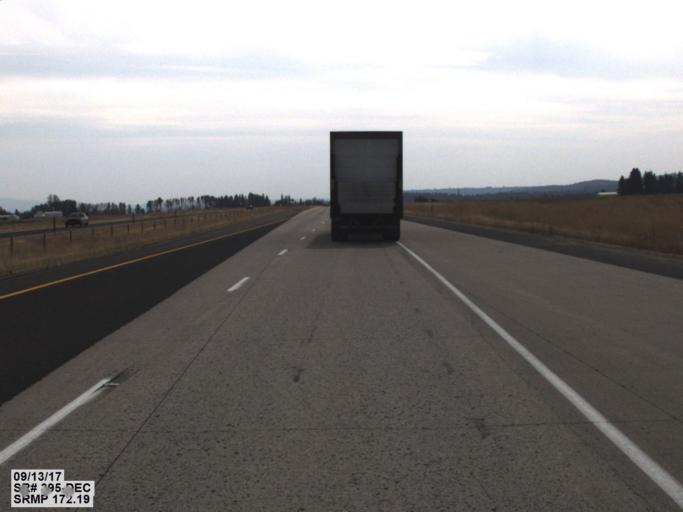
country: US
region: Washington
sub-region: Spokane County
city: Fairwood
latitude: 47.8473
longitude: -117.4221
